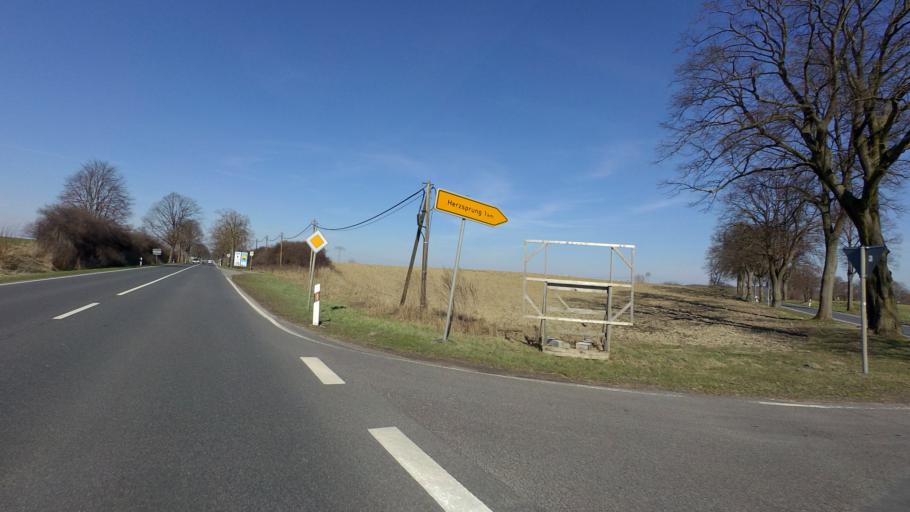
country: DE
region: Brandenburg
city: Angermunde
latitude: 52.9777
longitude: 13.9711
